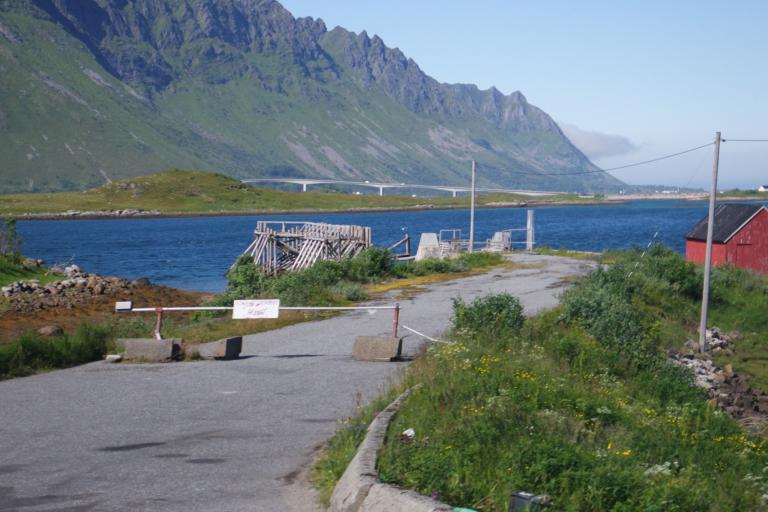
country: NO
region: Nordland
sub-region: Vagan
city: Kabelvag
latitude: 68.2396
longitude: 14.2572
